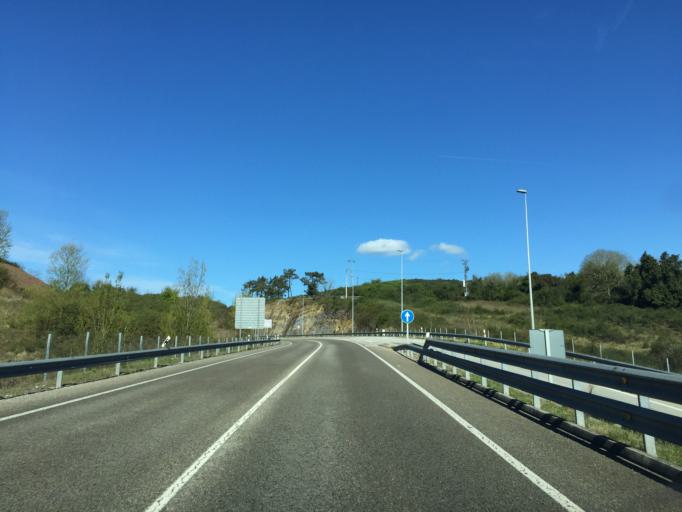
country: ES
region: Asturias
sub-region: Province of Asturias
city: Llanera
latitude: 43.3650
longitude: -5.9535
